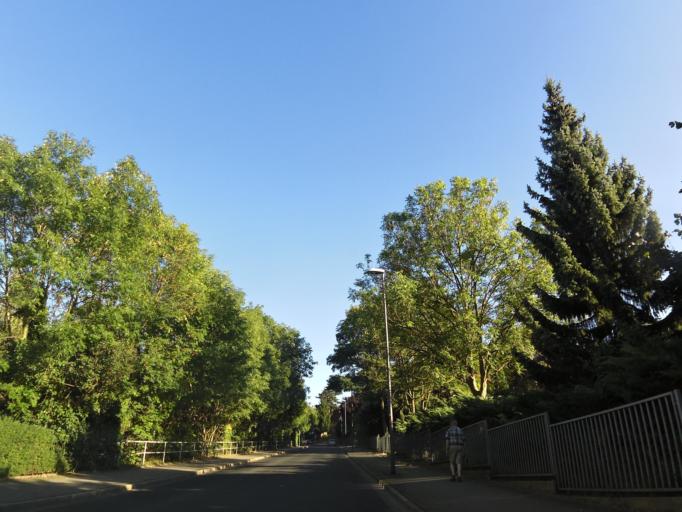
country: DE
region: Saxony
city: Dresden
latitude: 51.0130
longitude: 13.7695
